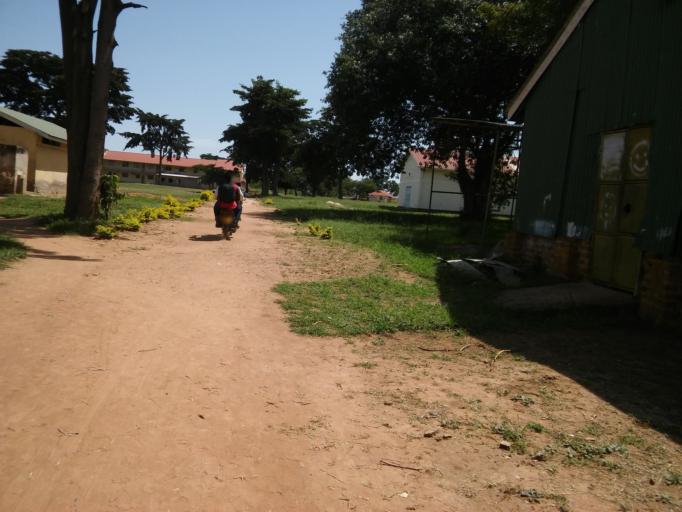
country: UG
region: Eastern Region
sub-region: Kumi District
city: Kumi
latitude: 1.4746
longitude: 33.8637
